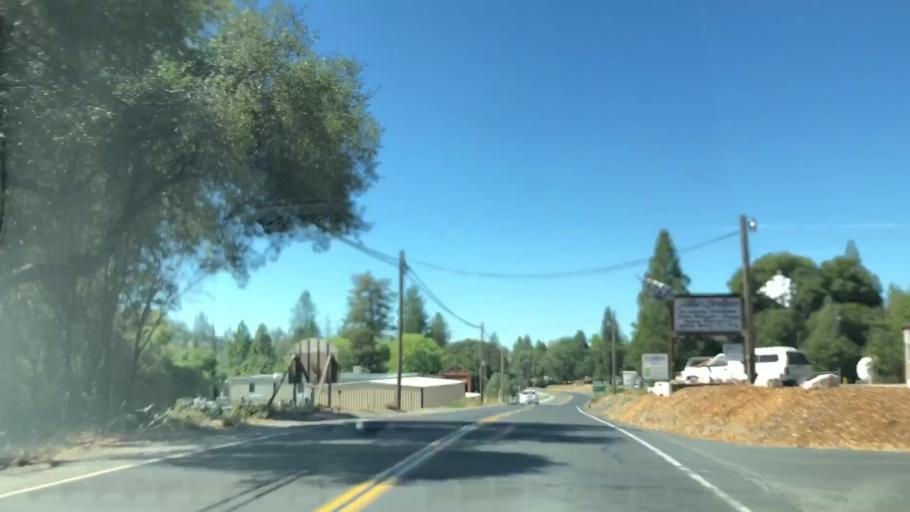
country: US
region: California
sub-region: Tuolumne County
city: Tuolumne City
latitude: 37.8281
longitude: -120.2502
